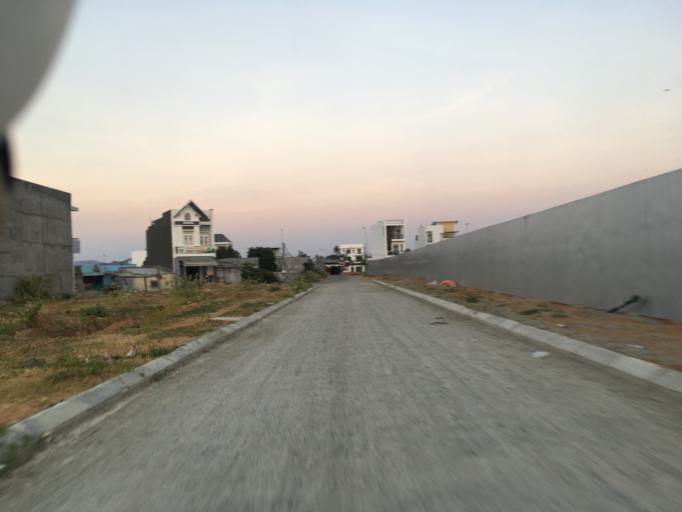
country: VN
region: Ninh Thuan
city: Phan Rang-Thap Cham
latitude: 11.5716
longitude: 108.9957
